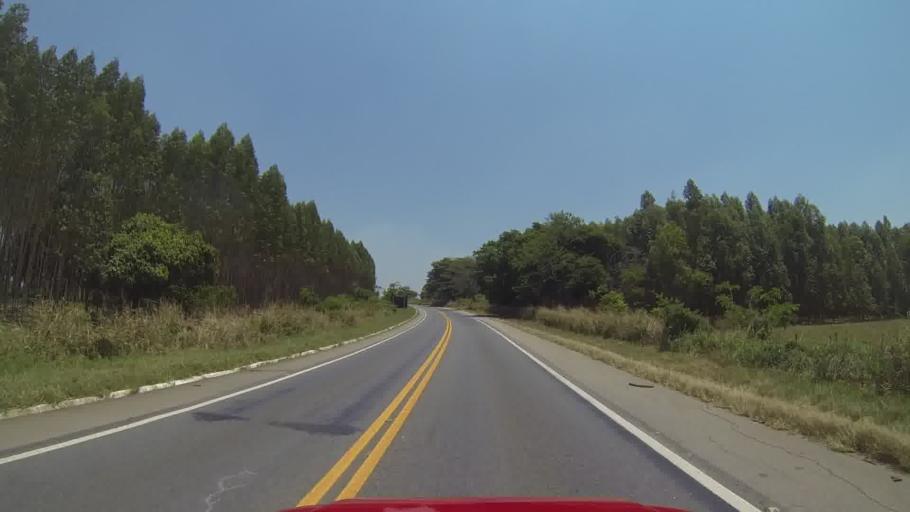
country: BR
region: Minas Gerais
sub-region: Itapecerica
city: Itapecerica
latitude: -20.3073
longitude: -45.2132
